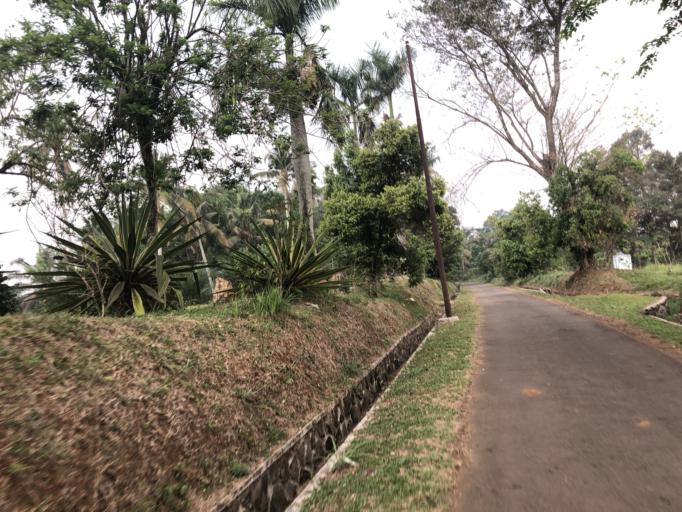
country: ID
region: West Java
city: Ciampea
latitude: -6.5520
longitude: 106.7164
